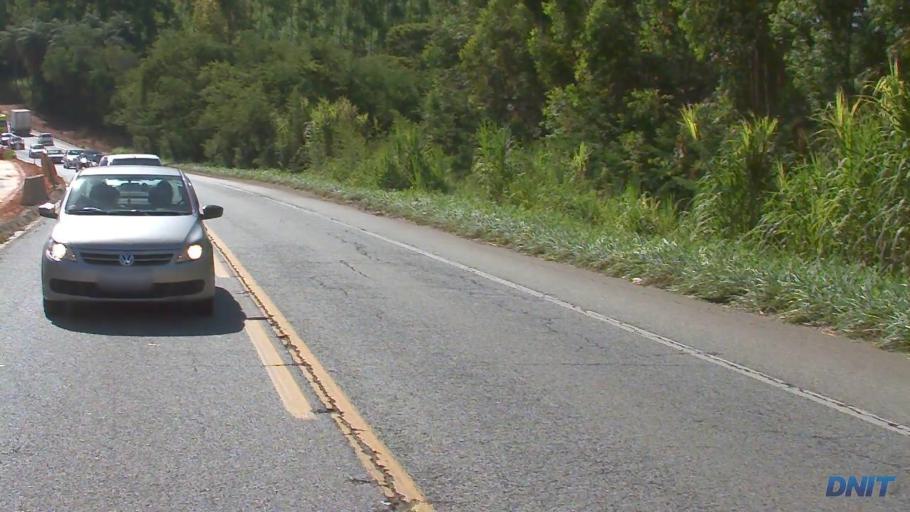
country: BR
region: Minas Gerais
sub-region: Caete
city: Caete
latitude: -19.7398
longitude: -43.6060
